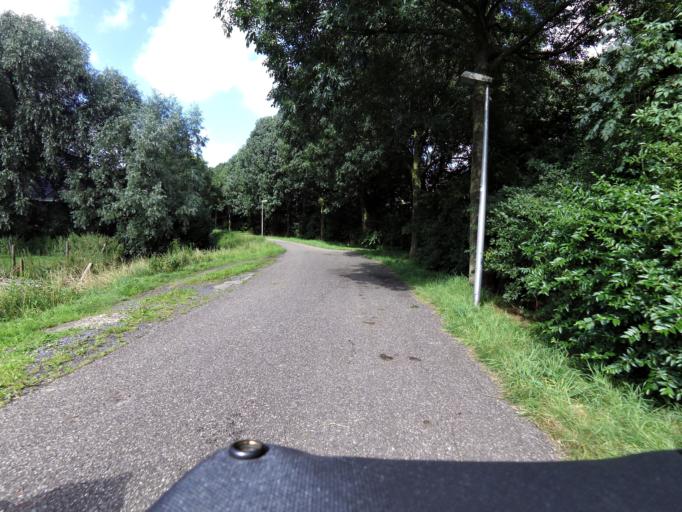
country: NL
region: South Holland
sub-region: Gemeente Spijkenisse
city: Spijkenisse
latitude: 51.8387
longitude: 4.3147
